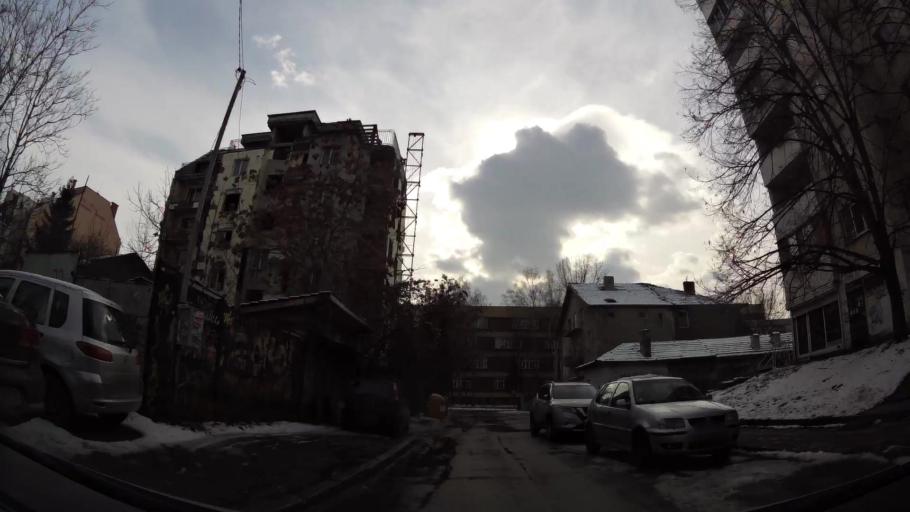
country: BG
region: Sofia-Capital
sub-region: Stolichna Obshtina
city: Sofia
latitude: 42.7078
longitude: 23.3591
